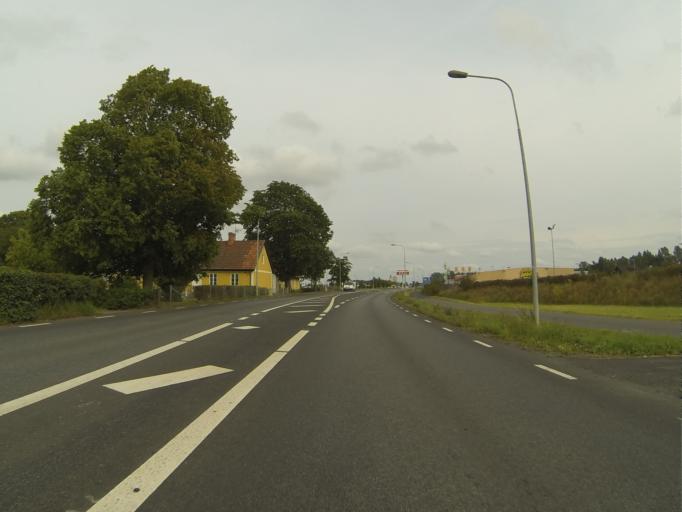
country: SE
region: Skane
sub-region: Kristianstads Kommun
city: Kristianstad
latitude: 56.0226
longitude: 14.1097
